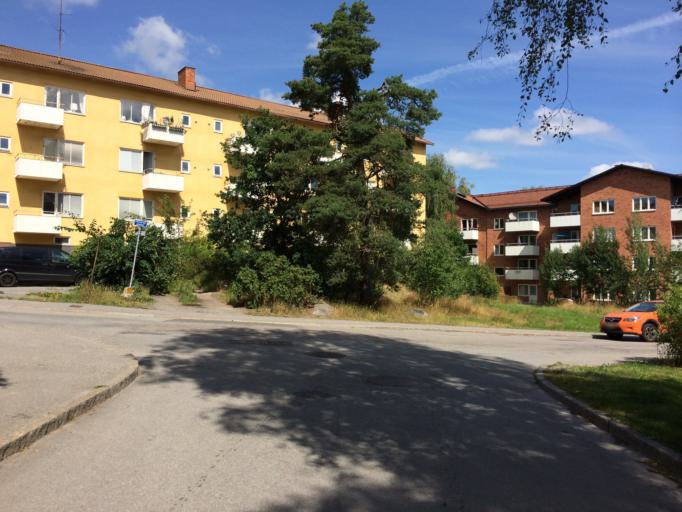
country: SE
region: Stockholm
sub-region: Huddinge Kommun
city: Huddinge
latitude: 59.2916
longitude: 17.9848
